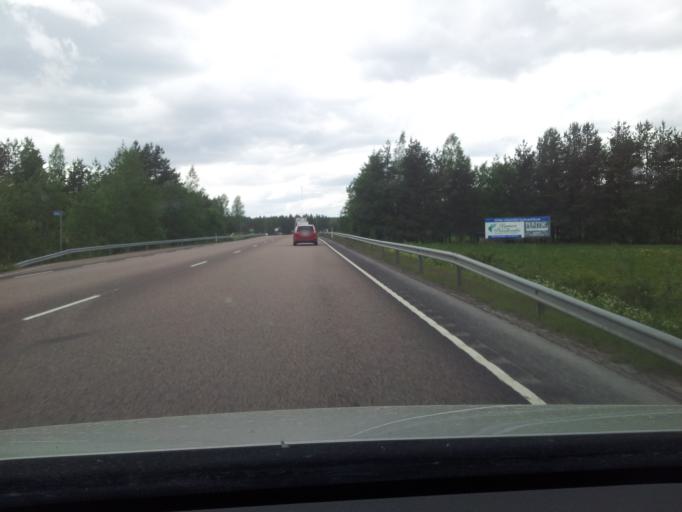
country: FI
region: Kymenlaakso
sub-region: Kotka-Hamina
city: Hamina
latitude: 60.9031
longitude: 27.1428
